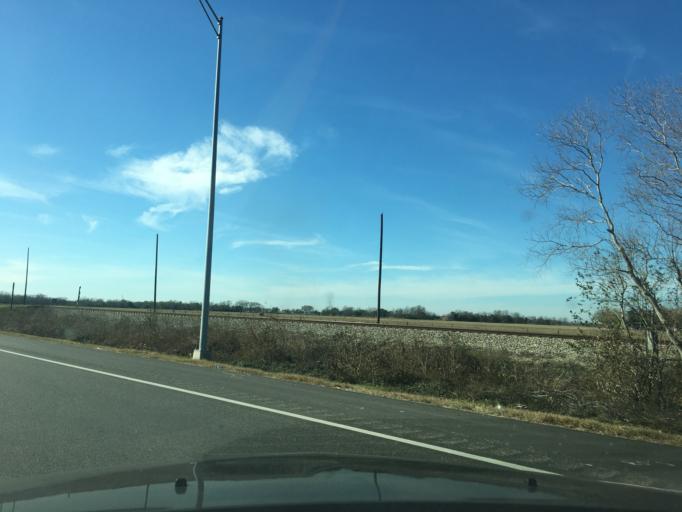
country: US
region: Texas
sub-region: Fort Bend County
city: Pleak
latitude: 29.4863
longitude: -95.9360
